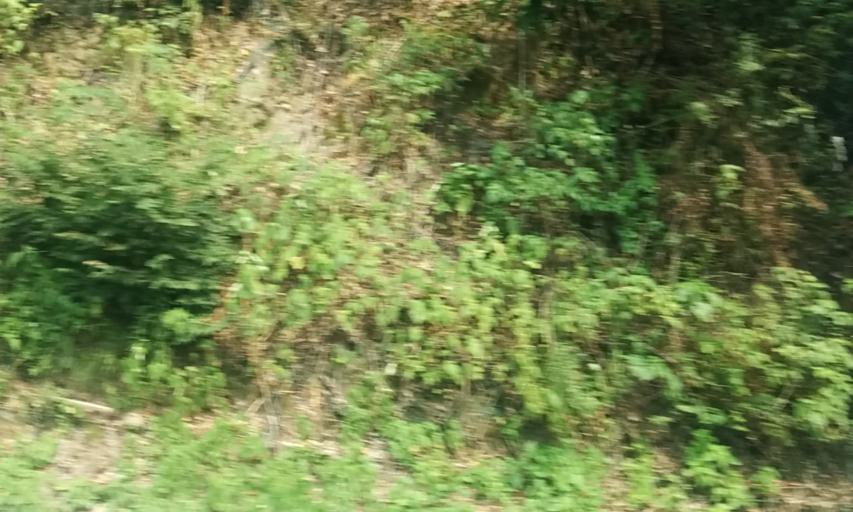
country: JP
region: Kyoto
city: Fukuchiyama
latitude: 35.3586
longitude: 135.1166
